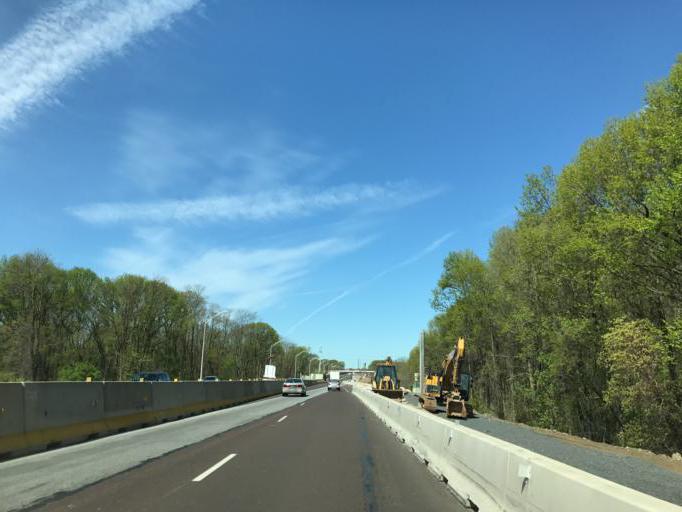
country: US
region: Pennsylvania
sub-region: Bucks County
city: Bristol
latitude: 40.1242
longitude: -74.8570
